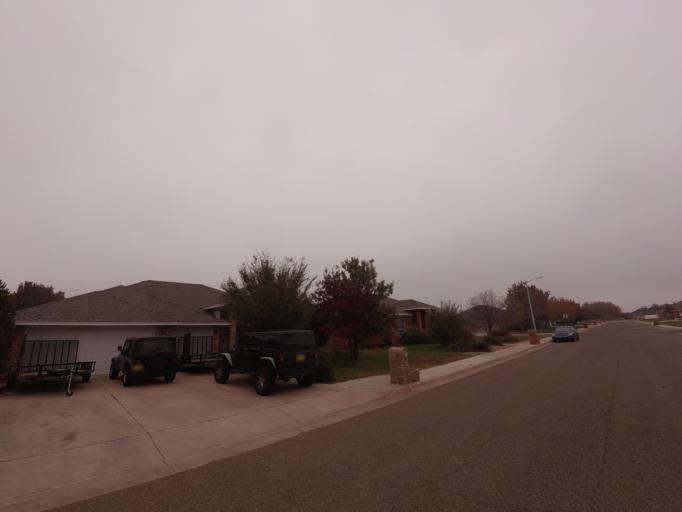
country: US
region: New Mexico
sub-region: Curry County
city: Clovis
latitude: 34.4312
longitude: -103.1701
